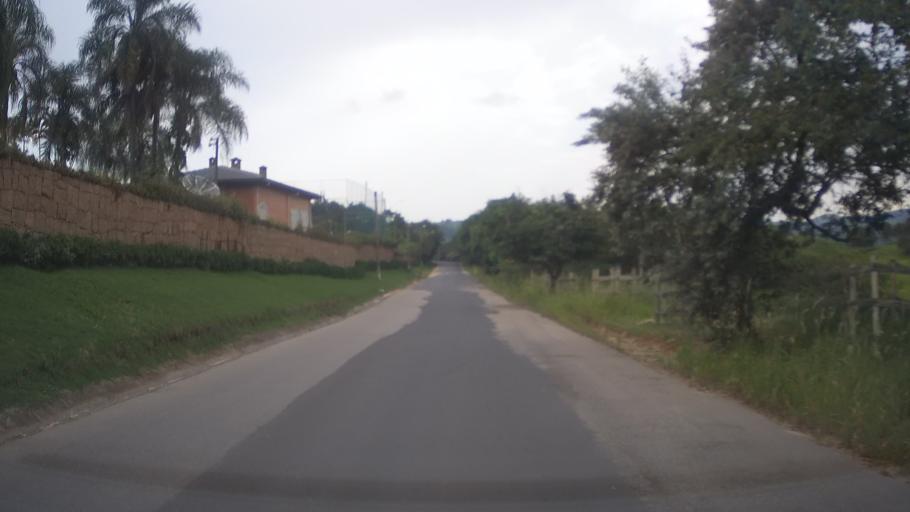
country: BR
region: Sao Paulo
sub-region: Itupeva
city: Itupeva
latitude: -23.1854
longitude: -47.0877
